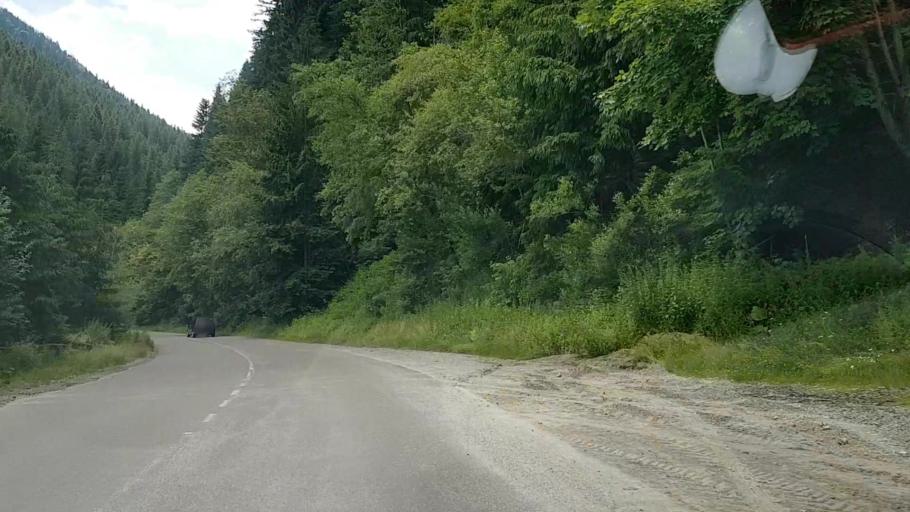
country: RO
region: Suceava
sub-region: Comuna Crucea
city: Crucea
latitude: 47.3517
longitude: 25.6057
